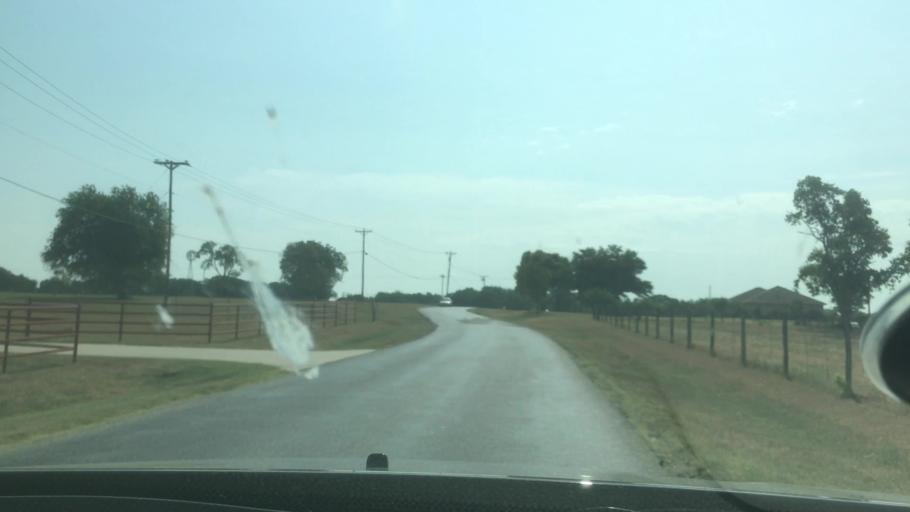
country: US
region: Texas
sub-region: Grayson County
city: Pottsboro
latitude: 33.8056
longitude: -96.7011
